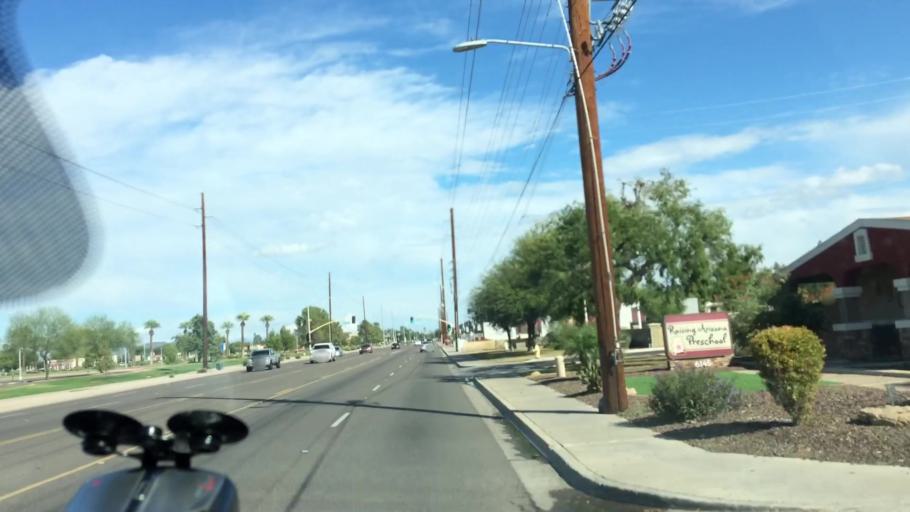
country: US
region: Arizona
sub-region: Maricopa County
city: Glendale
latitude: 33.5673
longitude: -112.1924
